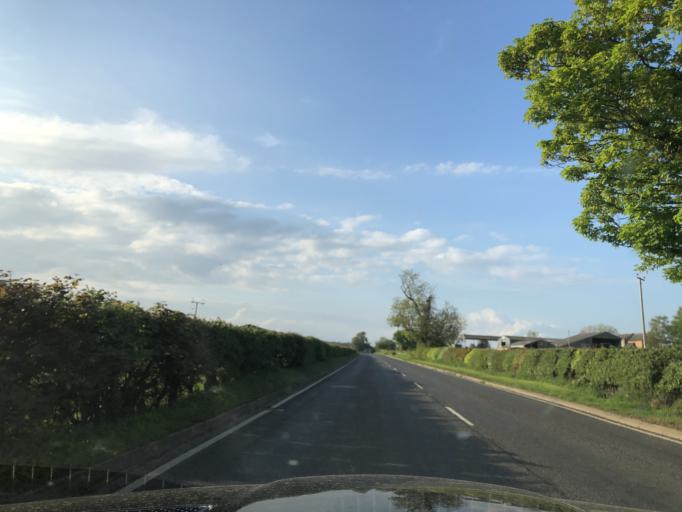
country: GB
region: England
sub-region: Warwickshire
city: Shipston on Stour
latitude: 52.1173
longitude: -1.6199
